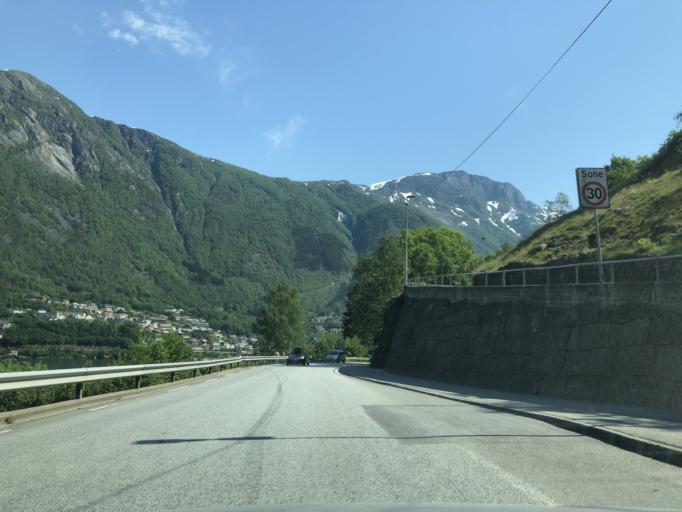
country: NO
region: Hordaland
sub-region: Odda
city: Odda
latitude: 60.0762
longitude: 6.5332
